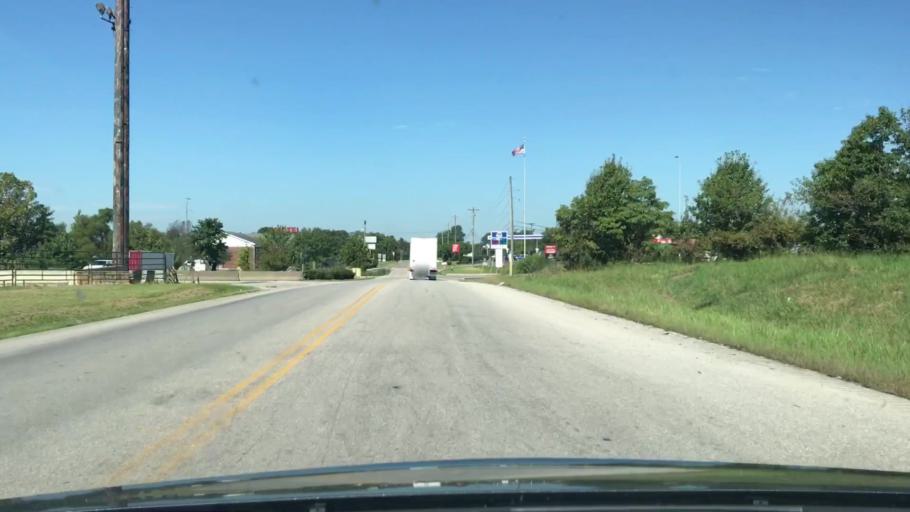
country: US
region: Kentucky
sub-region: Hardin County
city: Elizabethtown
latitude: 37.5970
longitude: -85.8711
